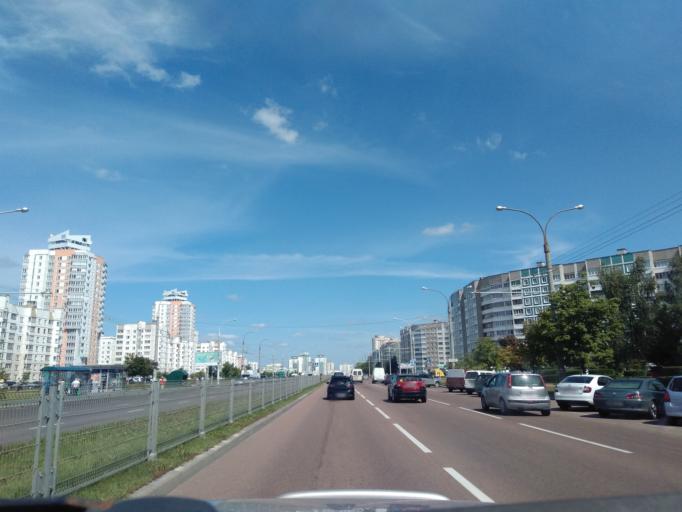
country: BY
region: Minsk
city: Novoye Medvezhino
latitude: 53.9109
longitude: 27.4363
